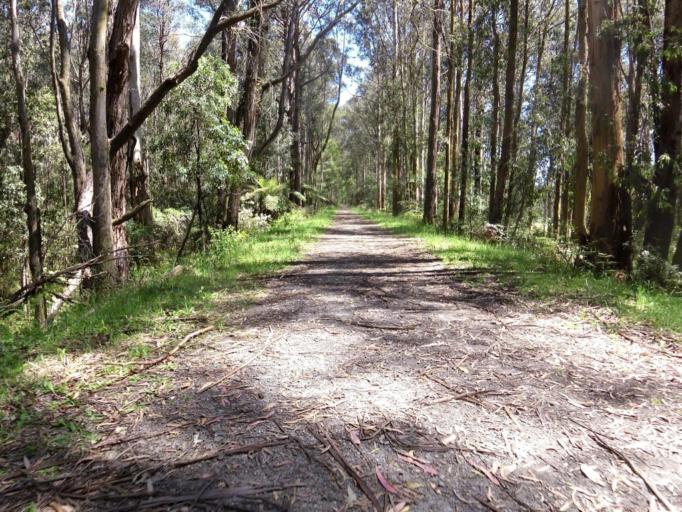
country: AU
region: Victoria
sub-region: Baw Baw
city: Warragul
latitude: -37.8958
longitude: 145.9922
